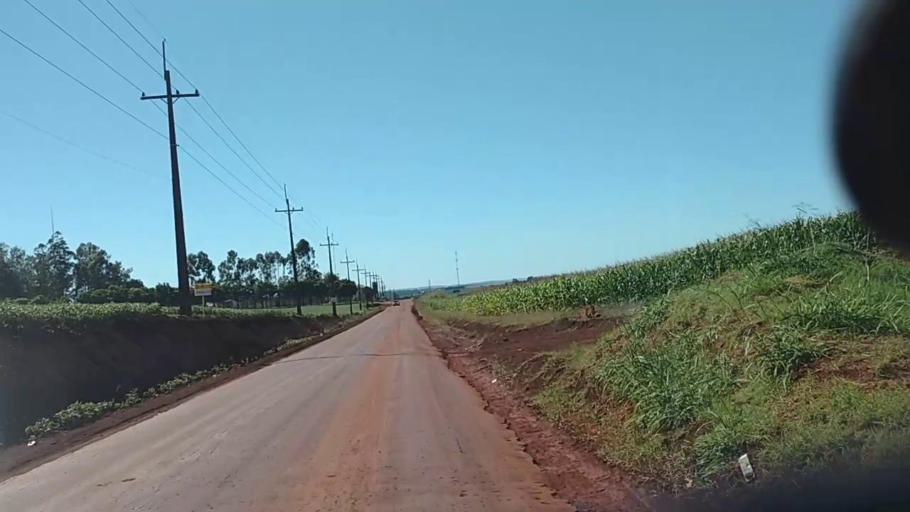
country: PY
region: Alto Parana
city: Naranjal
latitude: -25.9749
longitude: -55.2158
